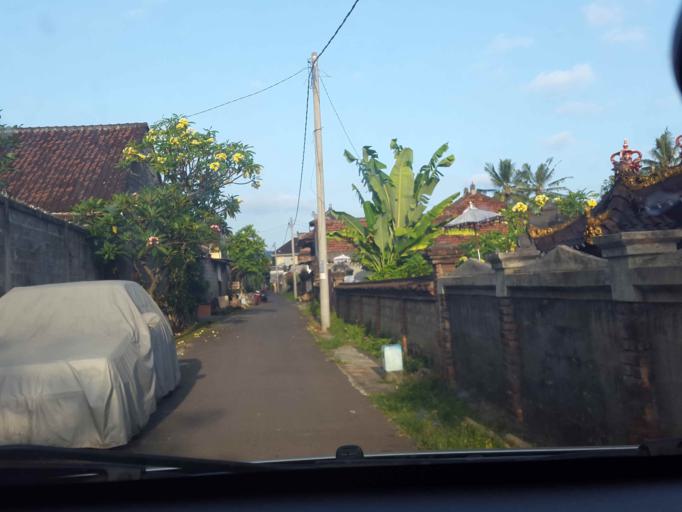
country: ID
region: Bali
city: Semarapura
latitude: -8.5406
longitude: 115.4134
